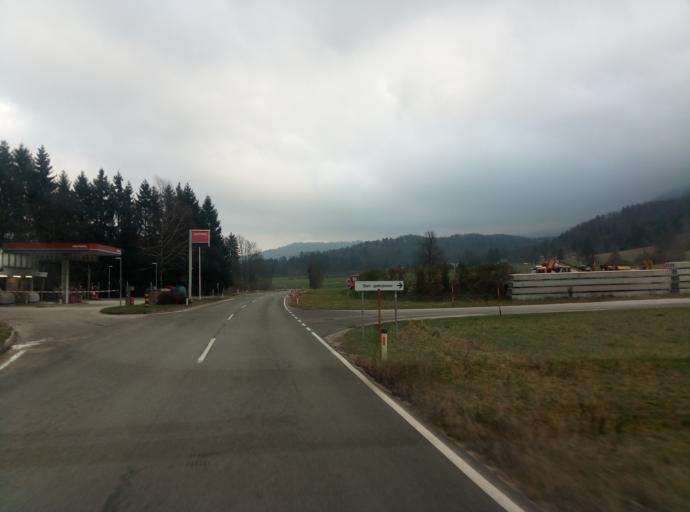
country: SI
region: Idrija
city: Idrija
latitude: 45.9257
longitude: 14.0526
